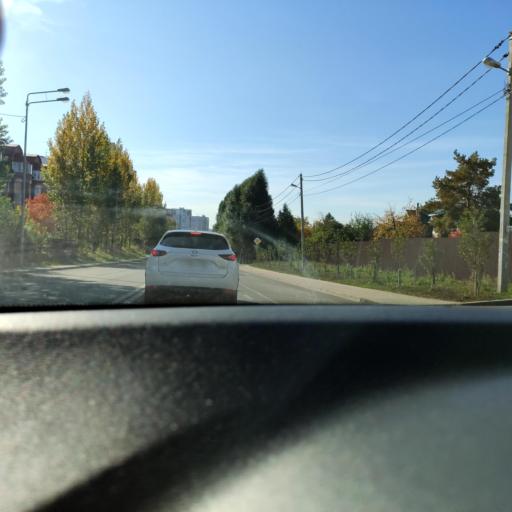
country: RU
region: Samara
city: Samara
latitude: 53.2684
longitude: 50.2148
